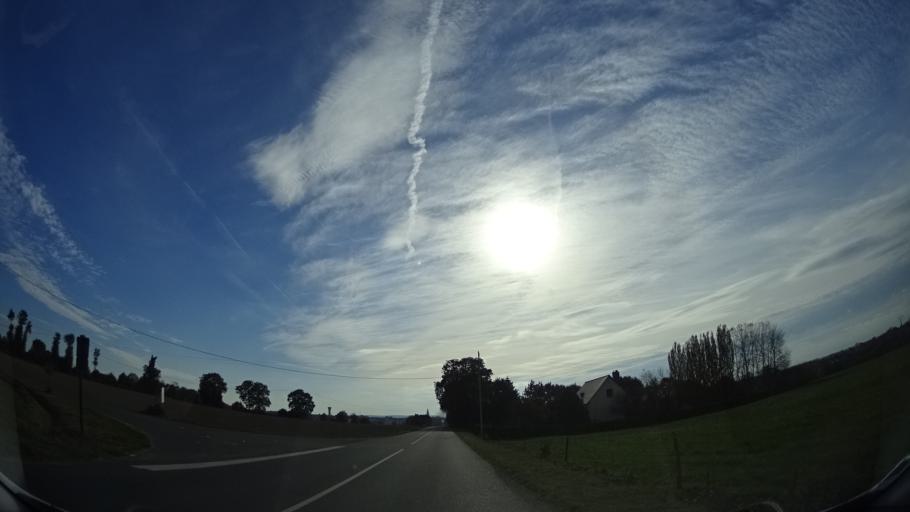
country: FR
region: Brittany
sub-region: Departement d'Ille-et-Vilaine
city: Bedee
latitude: 48.1979
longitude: -1.9398
